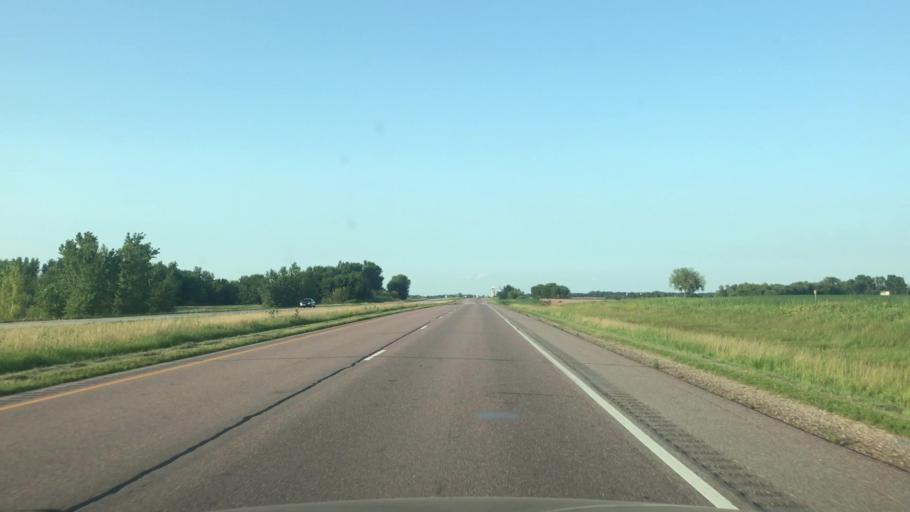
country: US
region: Minnesota
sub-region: Jackson County
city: Lakefield
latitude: 43.7723
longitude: -95.3578
